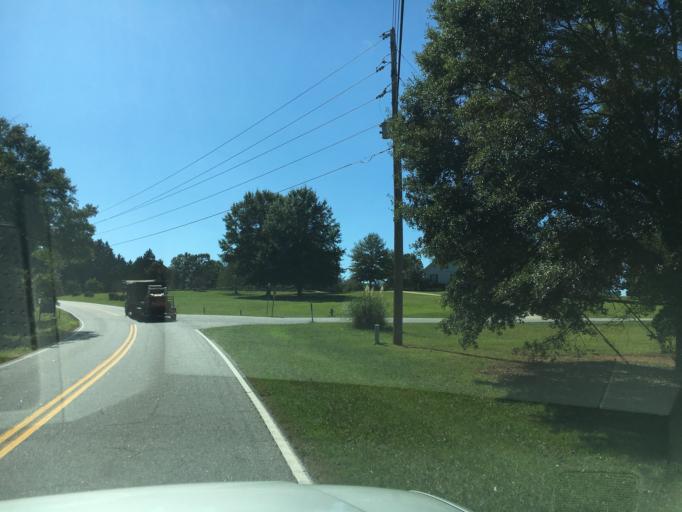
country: US
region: South Carolina
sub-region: Greenville County
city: Five Forks
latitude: 34.8212
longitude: -82.1999
